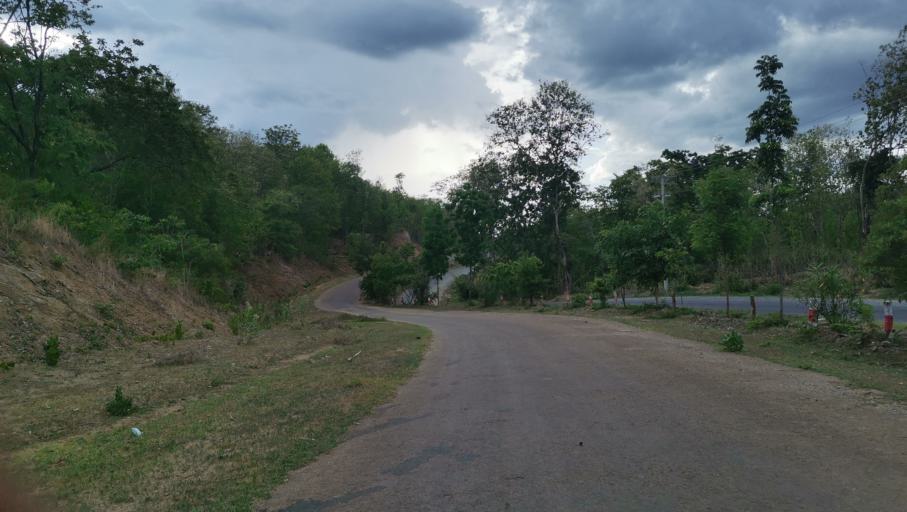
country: MM
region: Magway
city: Minbu
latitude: 20.1028
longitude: 94.5496
